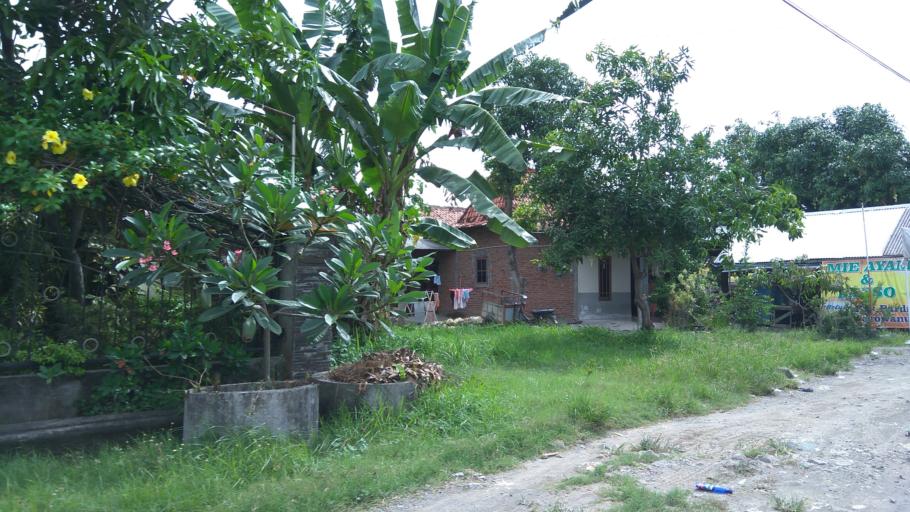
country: ID
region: Central Java
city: Mranggen
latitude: -7.0481
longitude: 110.5920
